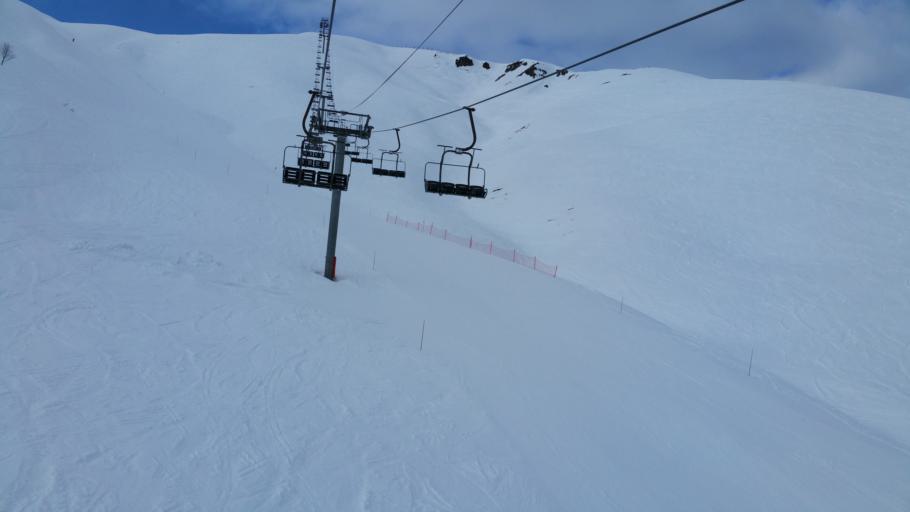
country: FR
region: Rhone-Alpes
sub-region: Departement de la Savoie
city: Saint-Etienne-de-Cuines
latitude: 45.2676
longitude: 6.2617
